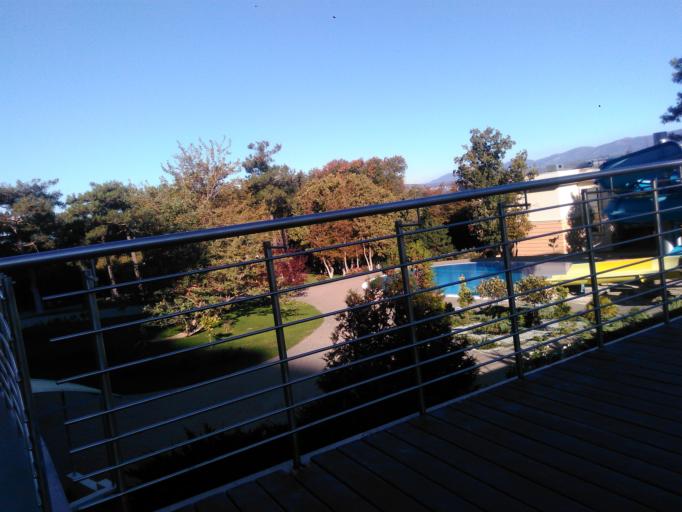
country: RU
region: Krasnodarskiy
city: Gelendzhik
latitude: 44.5519
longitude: 38.0546
